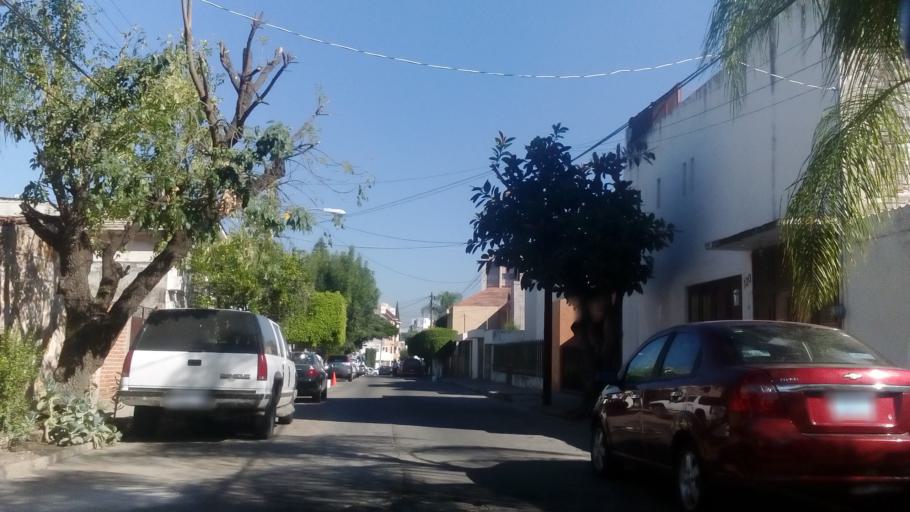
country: MX
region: Guanajuato
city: Leon
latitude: 21.1458
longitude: -101.6886
